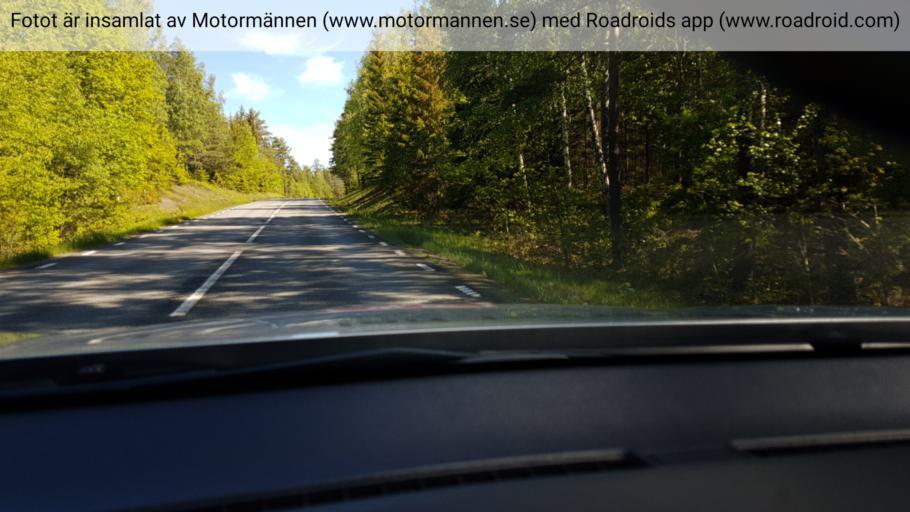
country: SE
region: Vaestra Goetaland
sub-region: Karlsborgs Kommun
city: Molltorp
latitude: 58.4158
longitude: 14.3784
